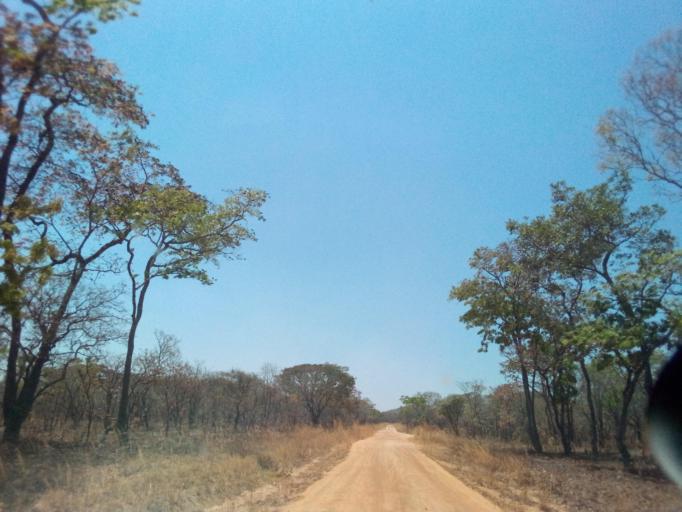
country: ZM
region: Northern
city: Mpika
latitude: -12.2540
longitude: 30.6903
